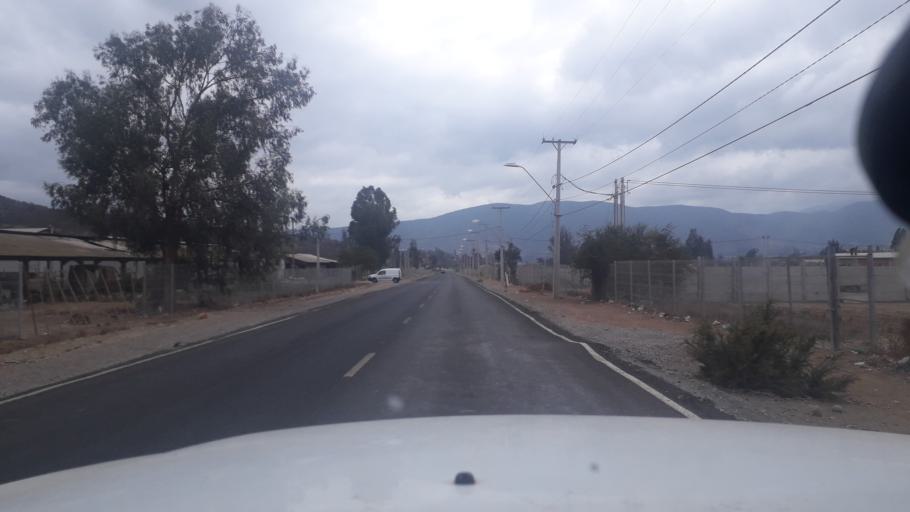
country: CL
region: Valparaiso
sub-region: Provincia de Marga Marga
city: Limache
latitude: -33.0233
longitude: -71.2747
